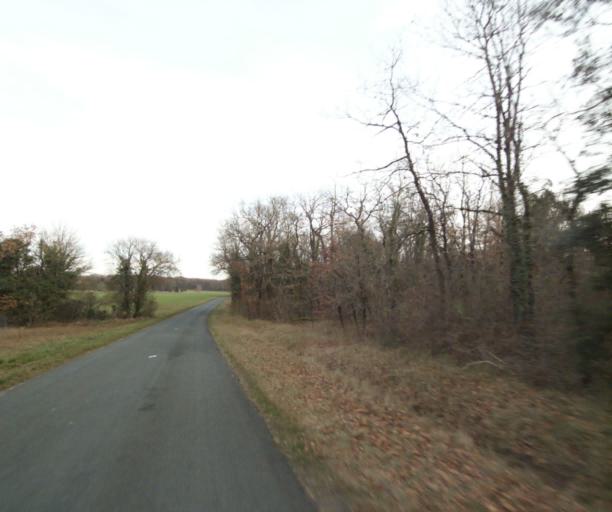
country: FR
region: Poitou-Charentes
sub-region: Departement de la Charente-Maritime
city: Fontcouverte
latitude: 45.8096
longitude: -0.5865
